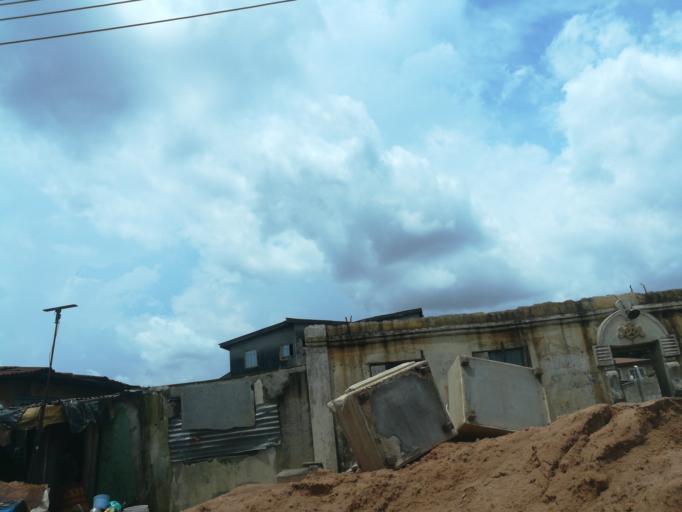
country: NG
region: Lagos
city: Somolu
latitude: 6.5423
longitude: 3.3613
